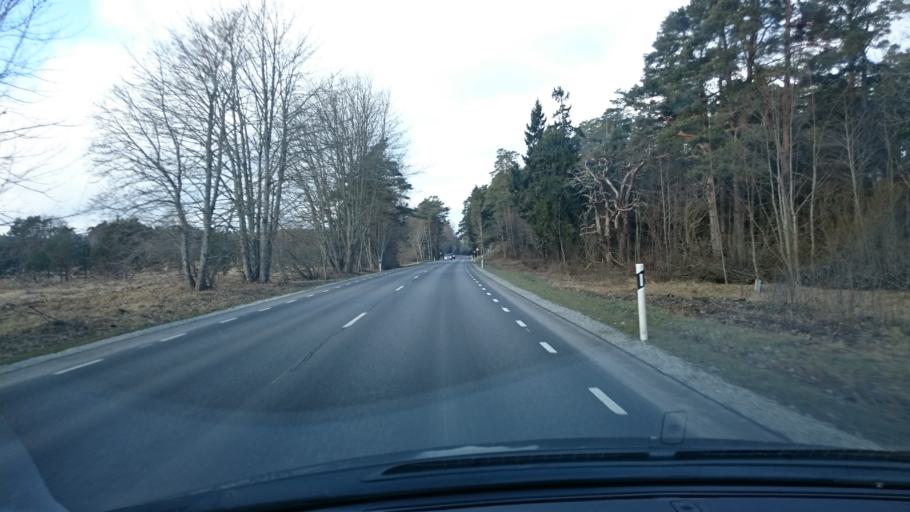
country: EE
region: Harju
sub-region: Keila linn
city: Keila
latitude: 59.3950
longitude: 24.2799
